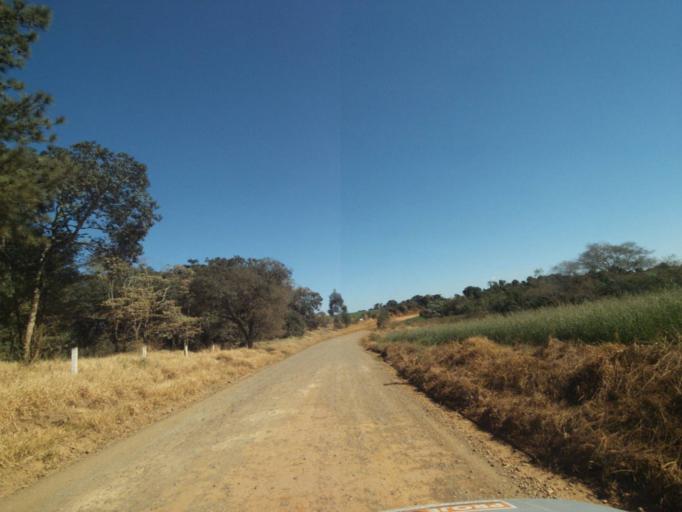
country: BR
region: Parana
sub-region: Reserva
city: Reserva
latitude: -24.6276
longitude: -50.6217
